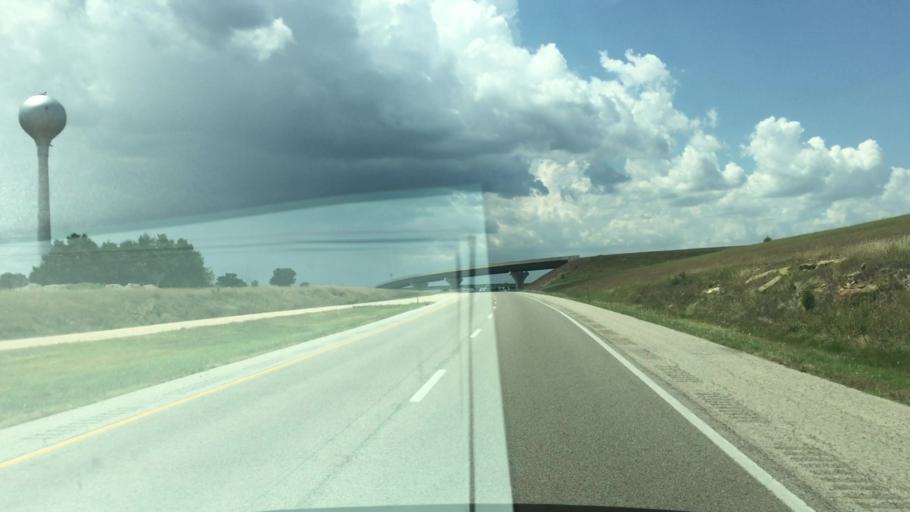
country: US
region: Kansas
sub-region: Shawnee County
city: Topeka
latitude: 39.0318
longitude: -95.6052
